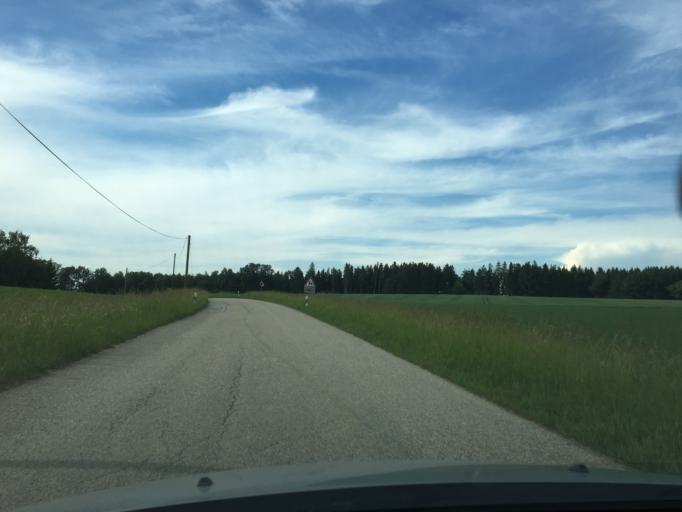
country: DE
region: Bavaria
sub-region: Upper Bavaria
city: Niedertaufkirchen
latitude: 48.3727
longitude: 12.5693
